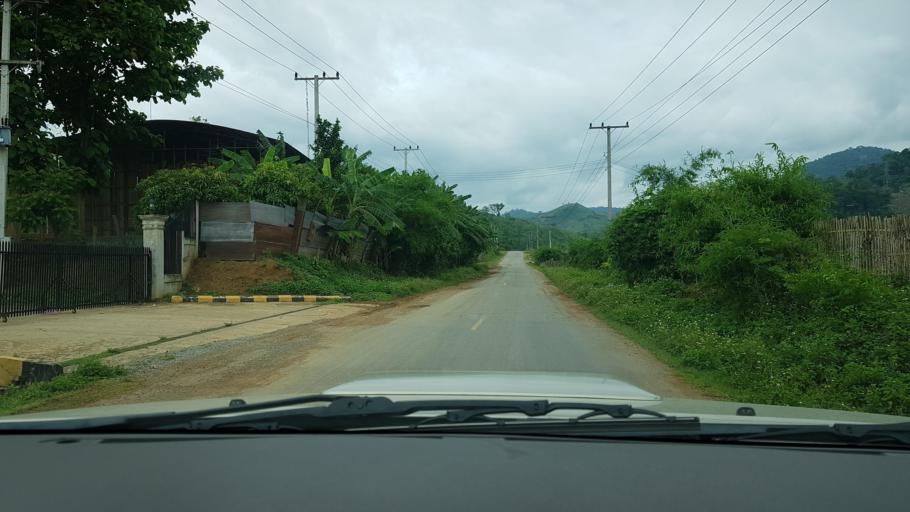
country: TH
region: Nan
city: Chaloem Phra Kiat
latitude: 19.9762
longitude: 101.2706
